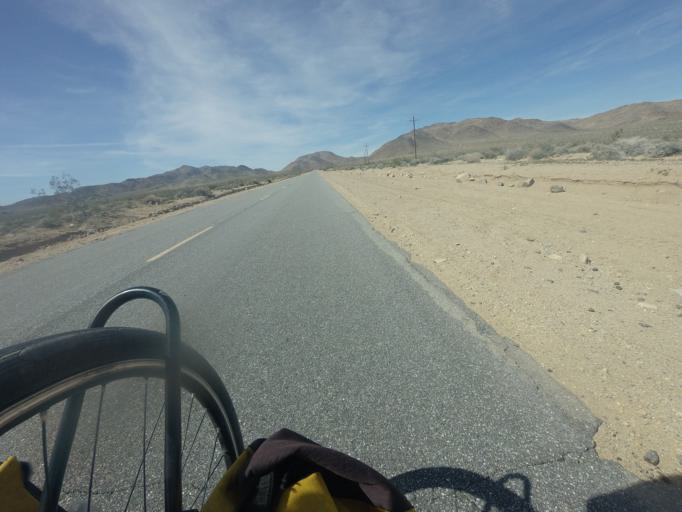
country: US
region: California
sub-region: San Bernardino County
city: Searles Valley
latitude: 35.5711
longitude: -117.4445
